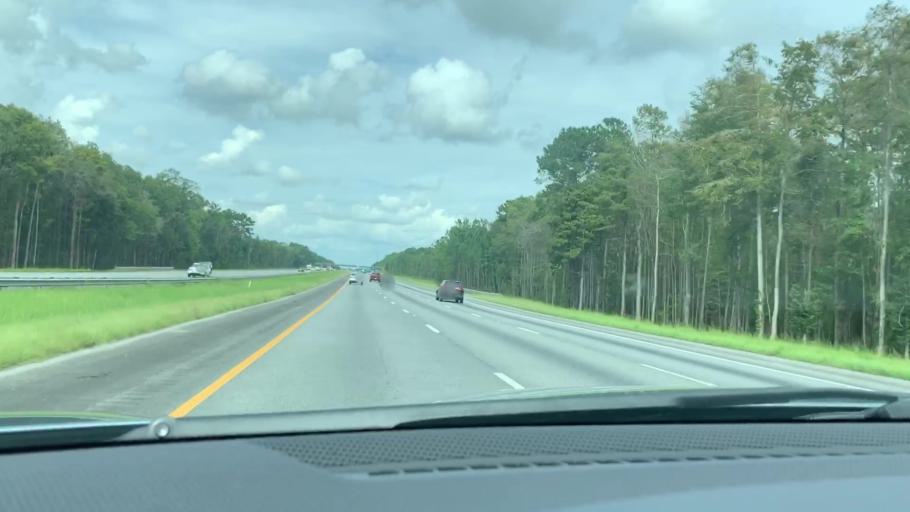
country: US
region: Georgia
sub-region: Liberty County
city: Midway
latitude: 31.6260
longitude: -81.4082
